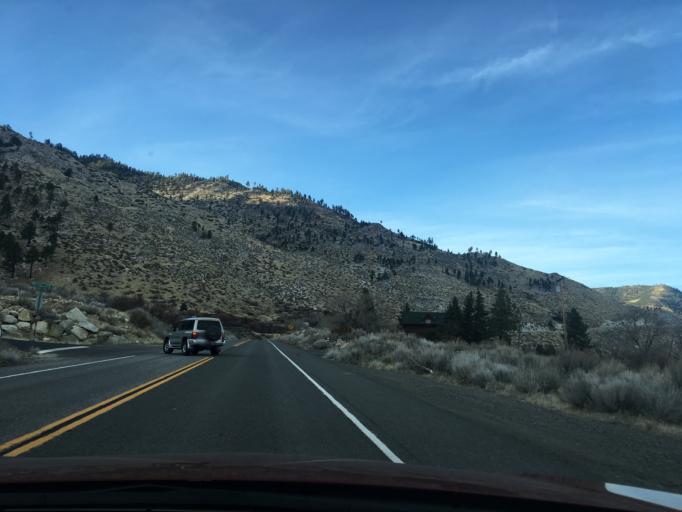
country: US
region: Nevada
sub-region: Douglas County
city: Kingsbury
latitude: 38.9309
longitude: -119.8440
